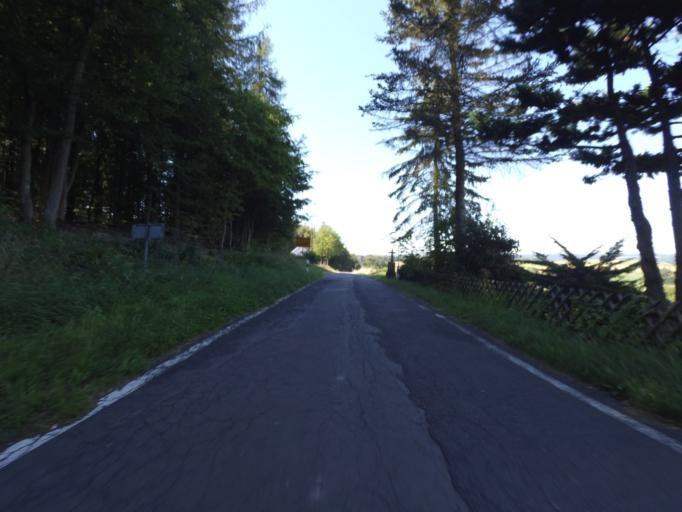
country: DE
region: Rheinland-Pfalz
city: Bad Bertrich
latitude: 50.0529
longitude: 7.0339
